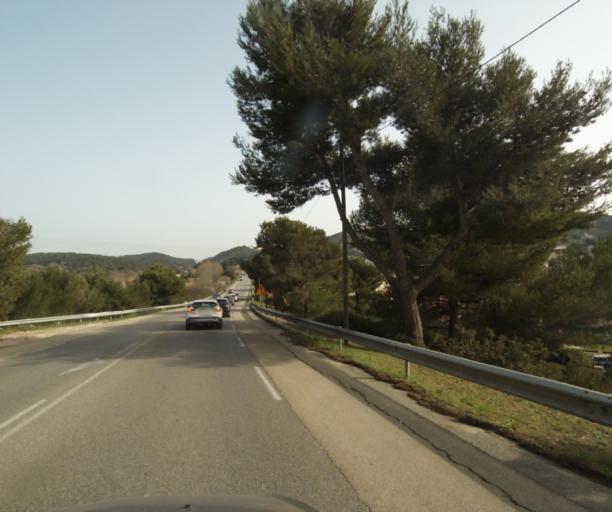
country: FR
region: Provence-Alpes-Cote d'Azur
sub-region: Departement des Bouches-du-Rhone
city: Les Pennes-Mirabeau
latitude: 43.4118
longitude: 5.3207
